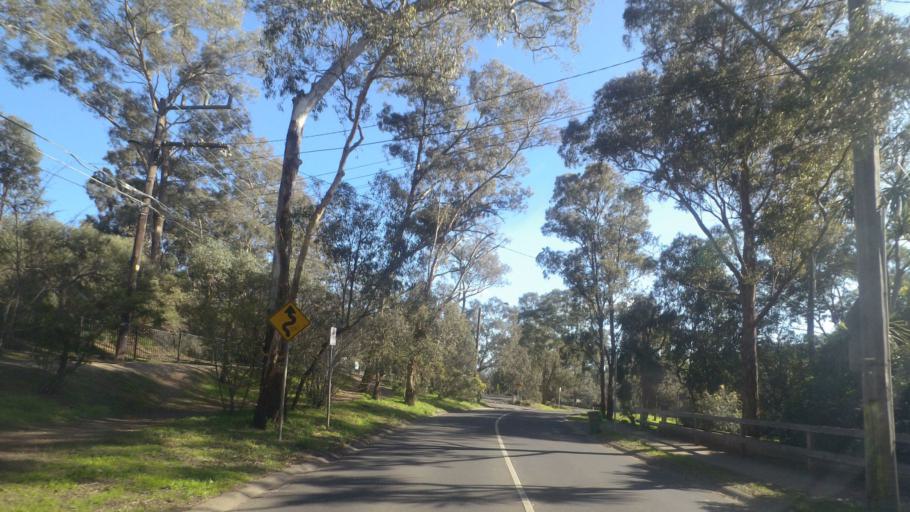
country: AU
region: Victoria
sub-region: Nillumbik
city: Eltham North
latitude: -37.7113
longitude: 145.1559
